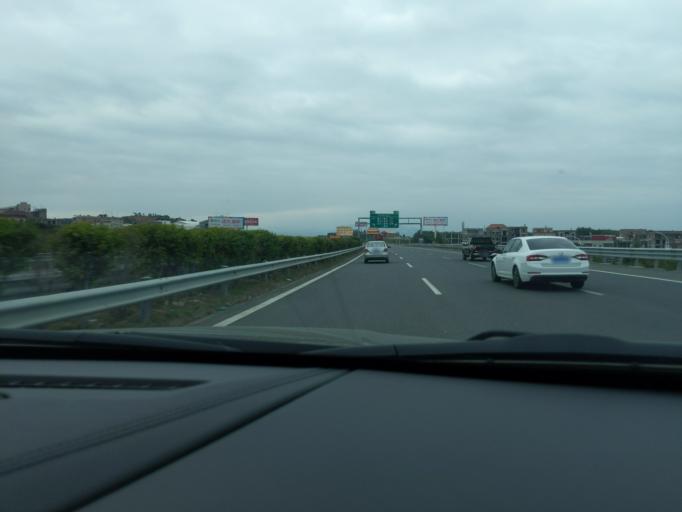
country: CN
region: Fujian
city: Cizao
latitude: 24.7809
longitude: 118.5054
